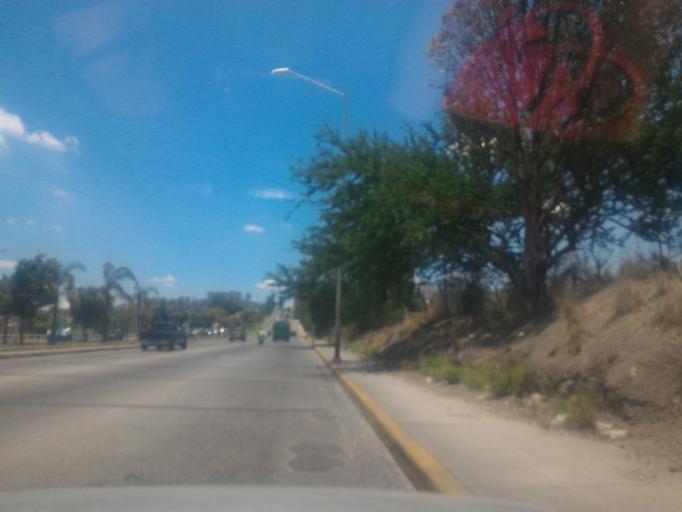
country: MX
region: Jalisco
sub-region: Tlajomulco de Zuniga
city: Altus Bosques
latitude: 20.5957
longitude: -103.3801
